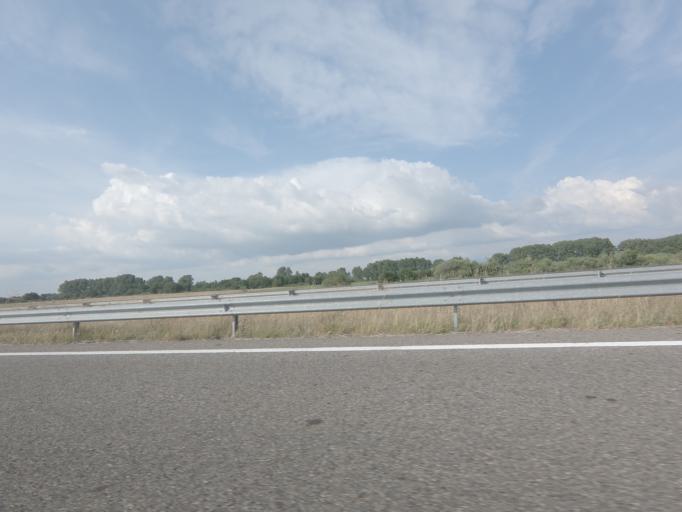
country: ES
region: Galicia
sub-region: Provincia de Ourense
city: Xinzo de Limia
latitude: 42.0831
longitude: -7.7162
